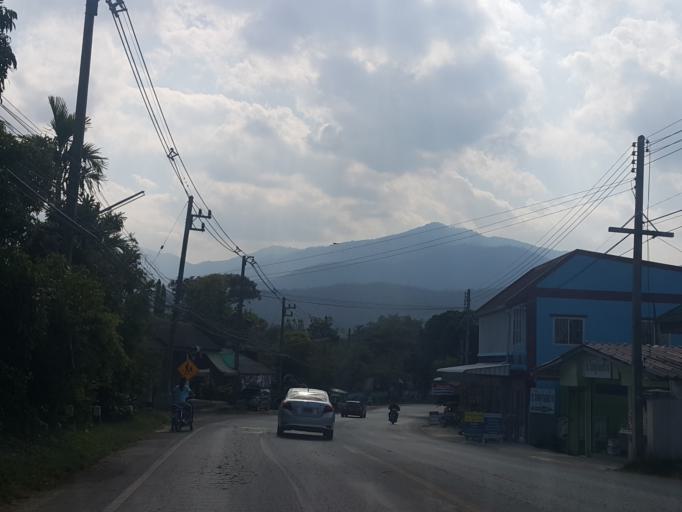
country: TH
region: Chiang Mai
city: Chiang Mai
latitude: 18.9167
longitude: 98.9092
